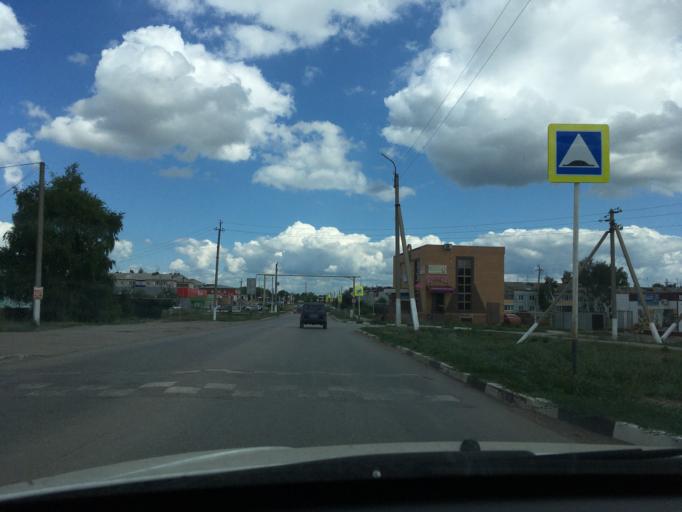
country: RU
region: Samara
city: Bezenchuk
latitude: 52.9919
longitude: 49.4369
